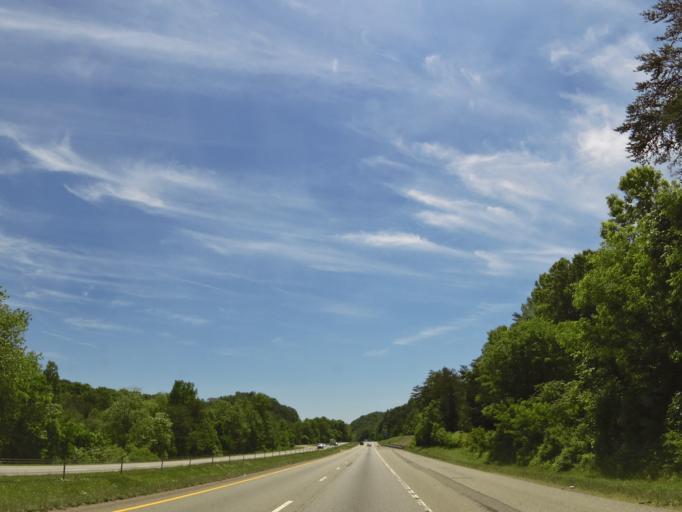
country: US
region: Tennessee
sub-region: Anderson County
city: Rocky Top
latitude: 36.2466
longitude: -84.1794
